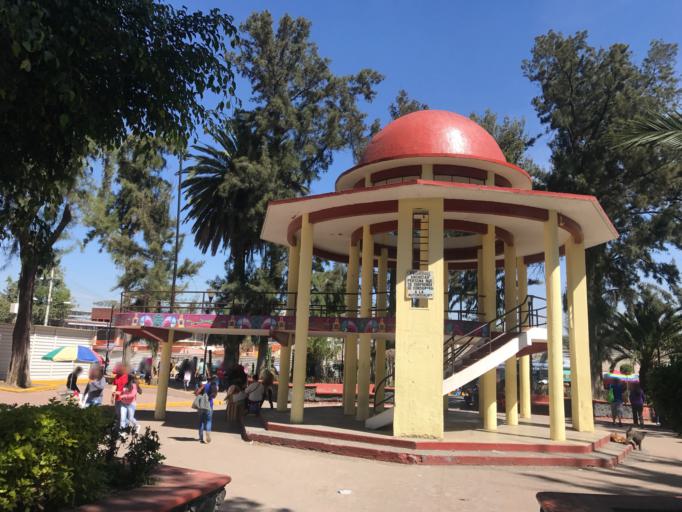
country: MX
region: Mexico City
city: Tlahuac
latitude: 19.2537
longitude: -99.0116
